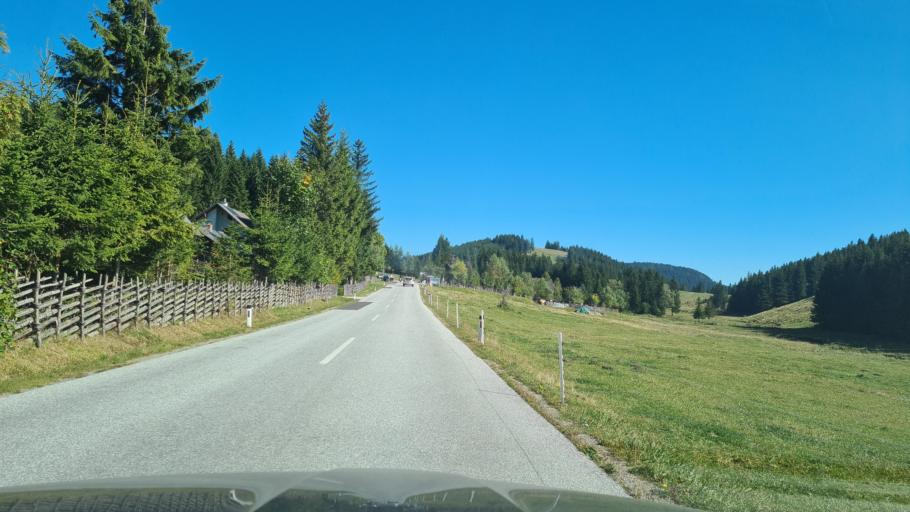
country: AT
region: Styria
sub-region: Politischer Bezirk Weiz
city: Gasen
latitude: 47.3527
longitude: 15.5061
